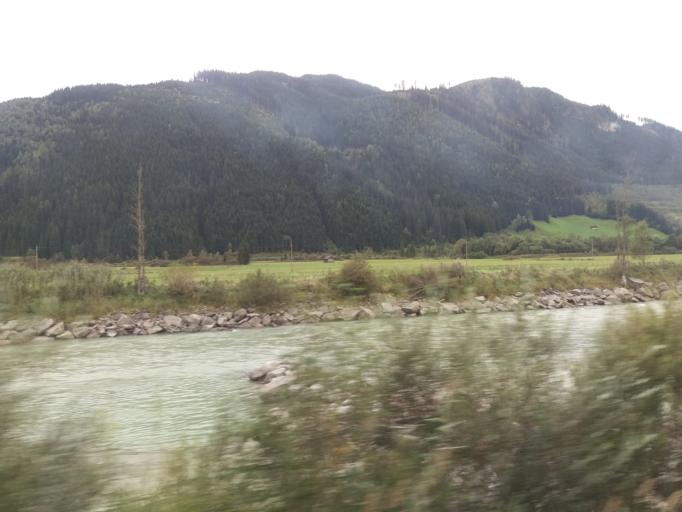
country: AT
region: Salzburg
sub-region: Politischer Bezirk Zell am See
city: Hollersbach im Pinzgau
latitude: 47.2791
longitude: 12.4094
